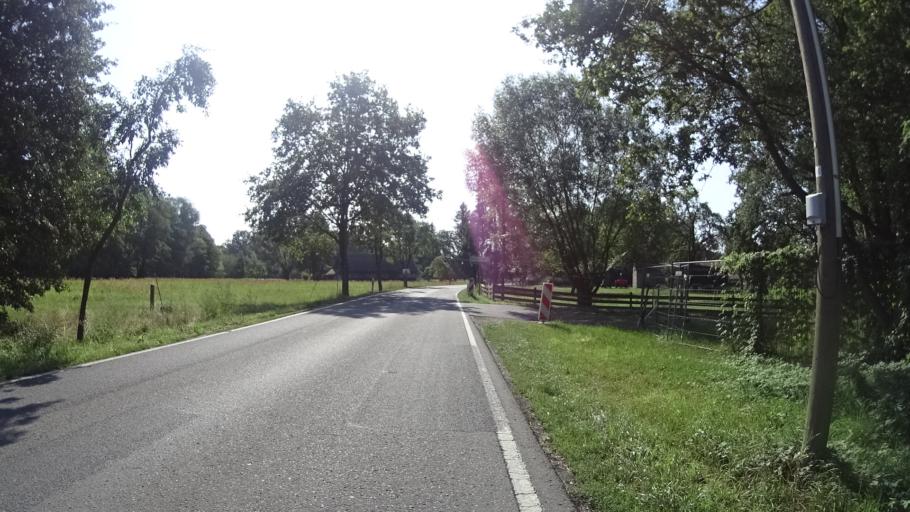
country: DE
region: Brandenburg
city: Burg
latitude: 51.8573
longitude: 14.1297
